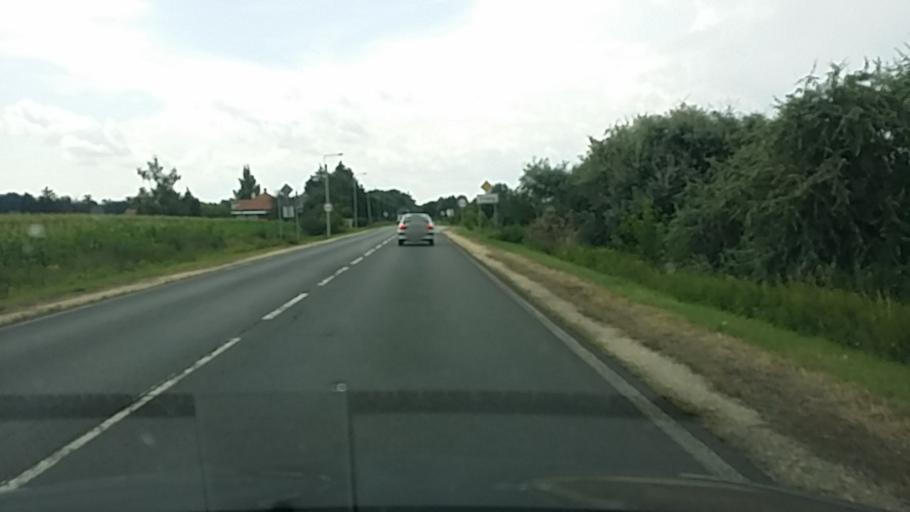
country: HU
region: Pest
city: Orkeny
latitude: 47.1207
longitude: 19.4396
